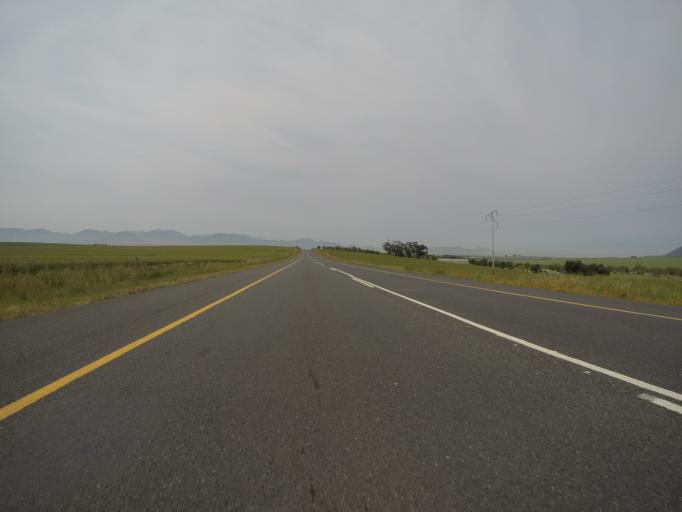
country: ZA
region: Western Cape
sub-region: West Coast District Municipality
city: Malmesbury
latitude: -33.5555
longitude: 18.8738
